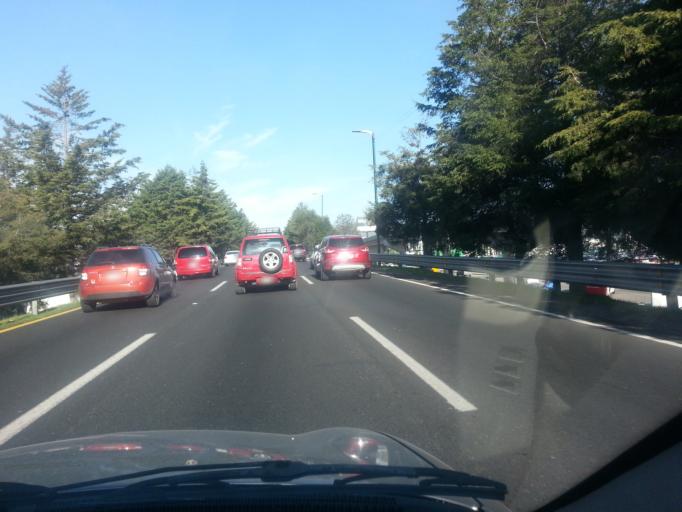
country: MX
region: Mexico
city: Santa Maria Totoltepec
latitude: 19.2878
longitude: -99.6099
